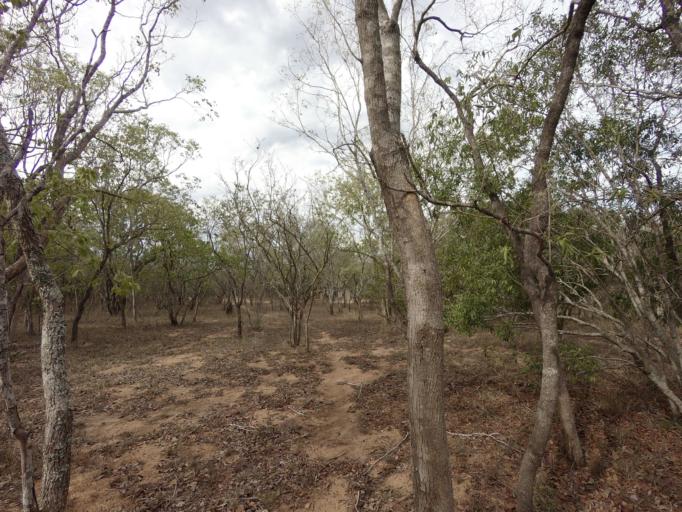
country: ZA
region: Limpopo
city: Thulamahashi
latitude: -24.5241
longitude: 31.1109
